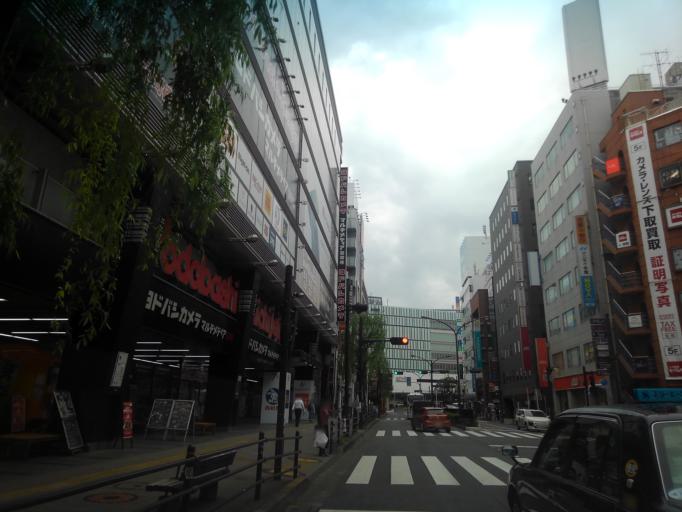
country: JP
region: Tokyo
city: Musashino
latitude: 35.7051
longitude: 139.5812
